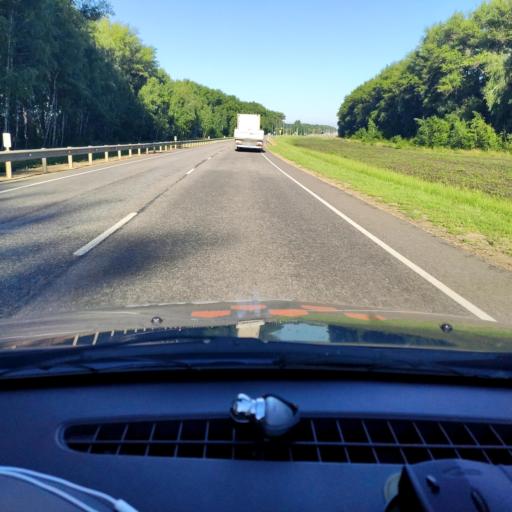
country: RU
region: Orjol
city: Zmiyevka
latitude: 52.6355
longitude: 36.6218
